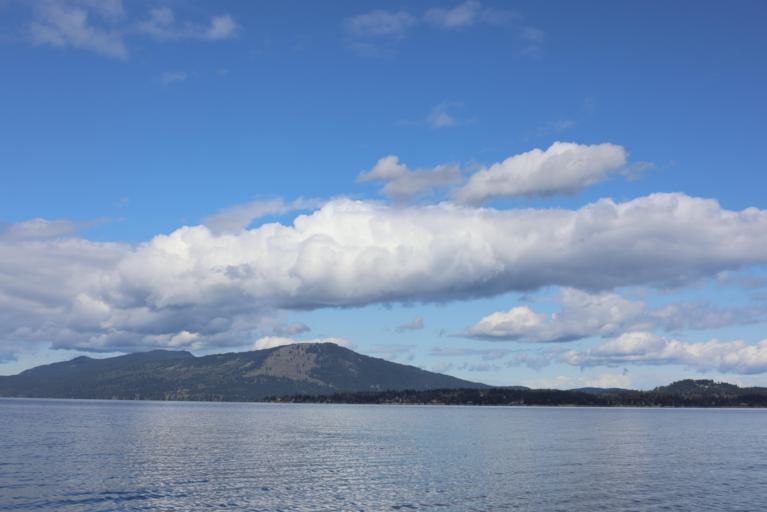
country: CA
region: British Columbia
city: North Saanich
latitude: 48.6267
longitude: -123.4861
